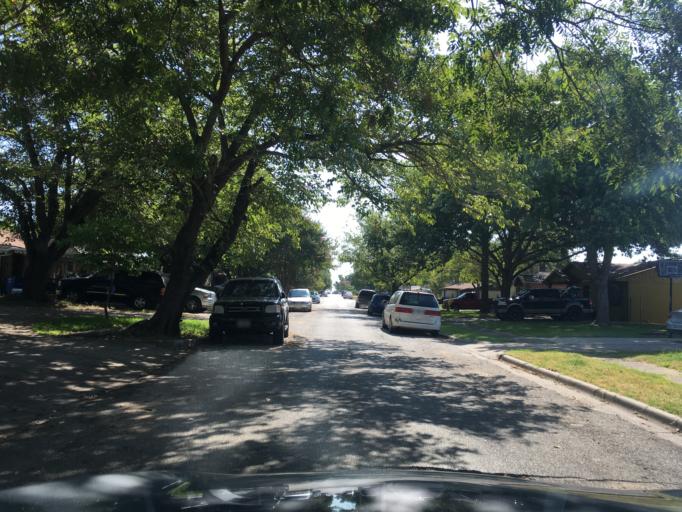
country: US
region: Texas
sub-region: Dallas County
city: Garland
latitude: 32.8550
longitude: -96.6739
